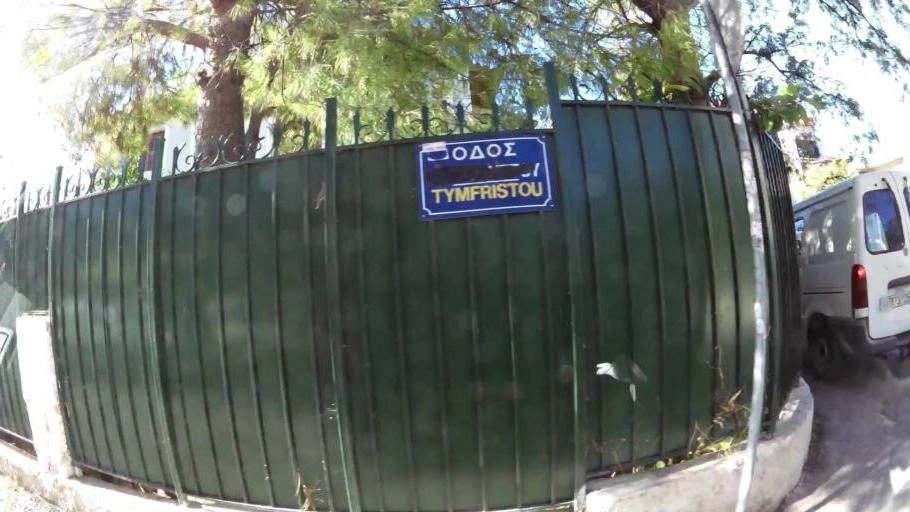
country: GR
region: Attica
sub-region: Nomarchia Athinas
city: Vrilissia
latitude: 38.0241
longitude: 23.8173
